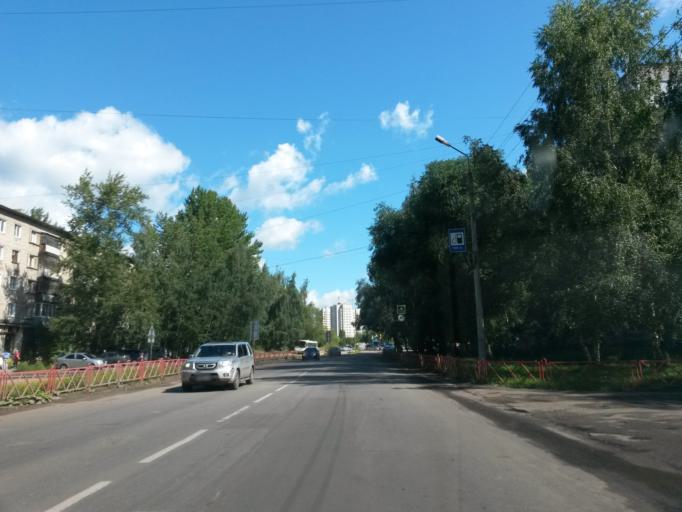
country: RU
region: Jaroslavl
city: Yaroslavl
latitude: 57.5733
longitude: 39.8618
